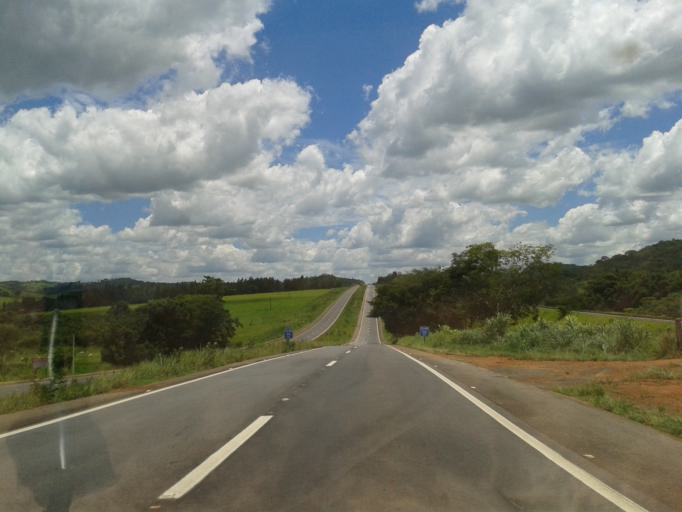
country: BR
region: Goias
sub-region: Petrolina De Goias
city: Petrolina de Goias
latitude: -16.1645
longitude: -49.3350
